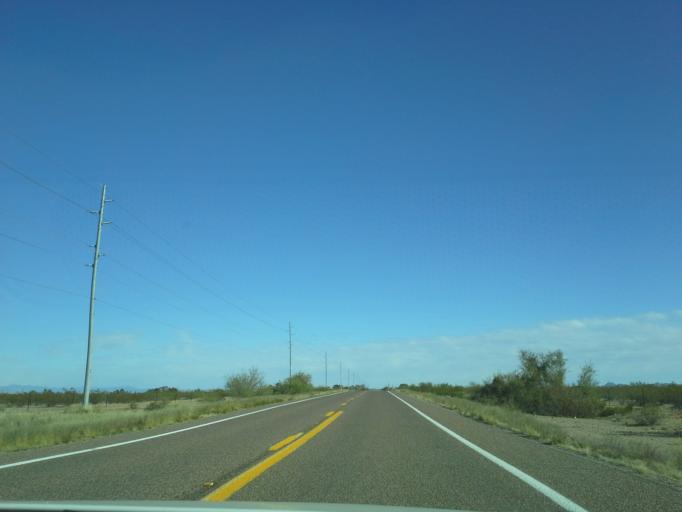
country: US
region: Arizona
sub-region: Yavapai County
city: Congress
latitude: 33.9429
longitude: -113.0217
